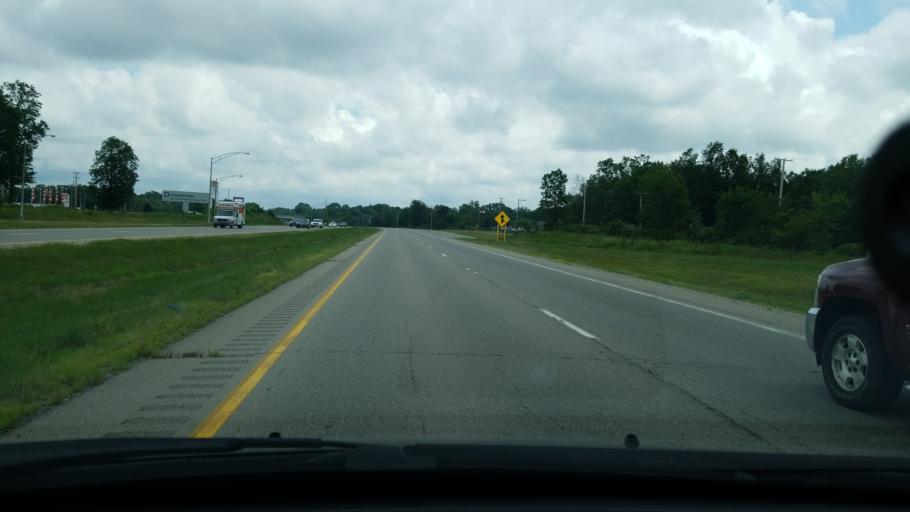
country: US
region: Ohio
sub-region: Lorain County
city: Amherst
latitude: 41.4107
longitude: -82.2368
